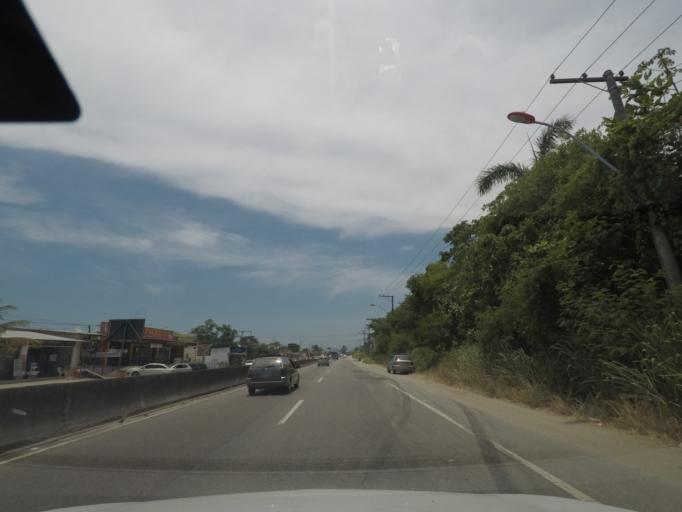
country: BR
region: Rio de Janeiro
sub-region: Marica
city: Marica
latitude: -22.9346
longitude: -42.8992
